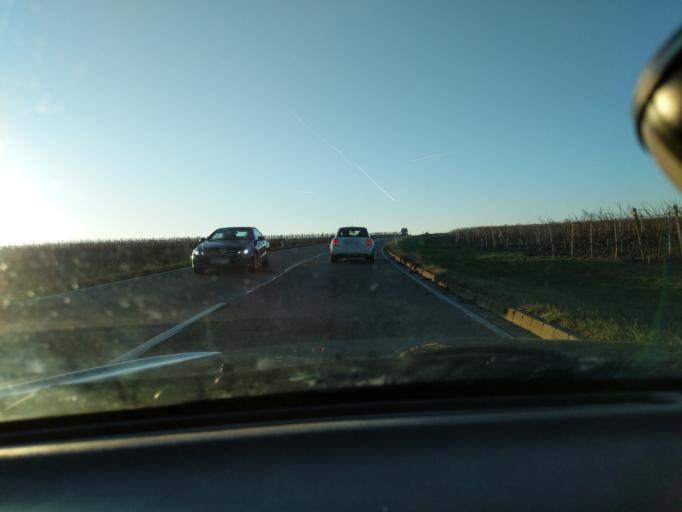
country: DE
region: Rheinland-Pfalz
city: Dackenheim
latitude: 49.5186
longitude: 8.1794
